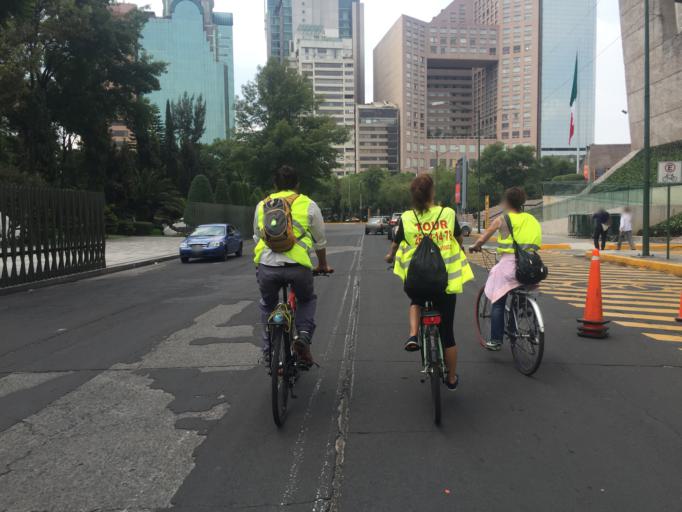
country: MX
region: Mexico City
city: Polanco
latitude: 19.4249
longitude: -99.1956
